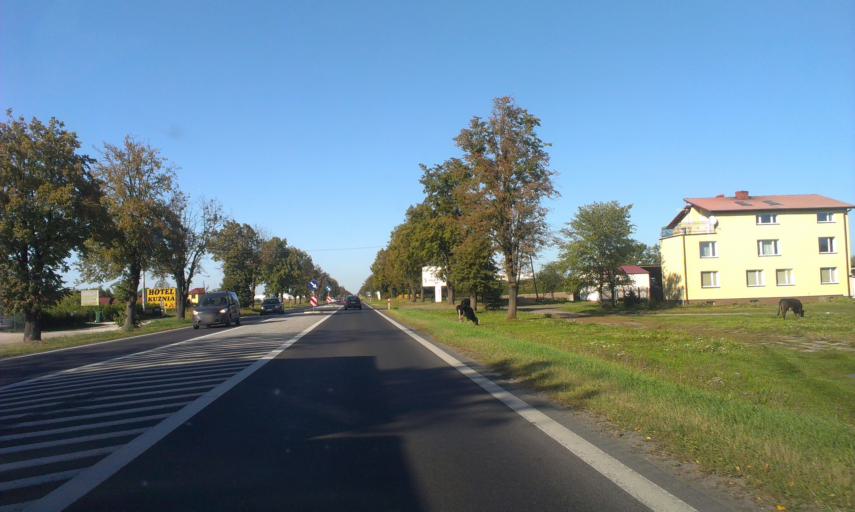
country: PL
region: Kujawsko-Pomorskie
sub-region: Powiat torunski
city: Lysomice
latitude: 53.0930
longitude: 18.6212
